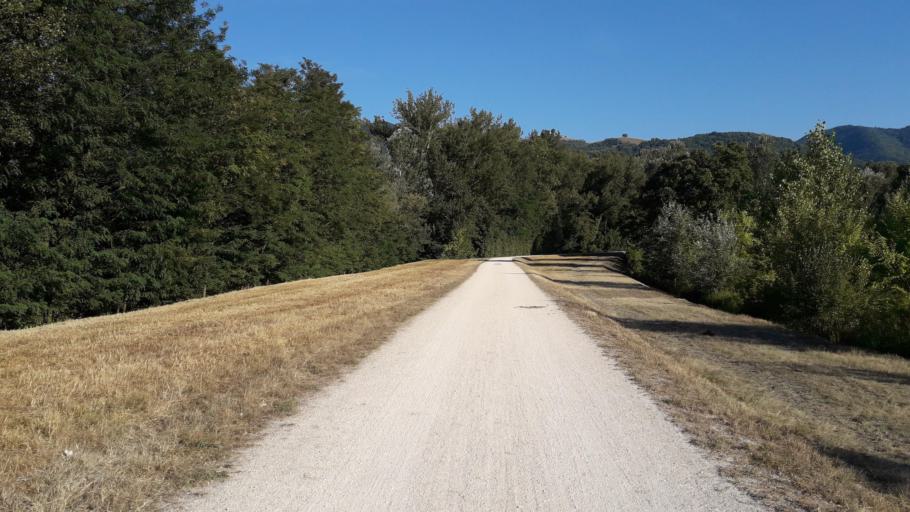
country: FR
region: Rhone-Alpes
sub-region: Departement de l'Isere
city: Gieres
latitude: 45.2016
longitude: 5.7973
